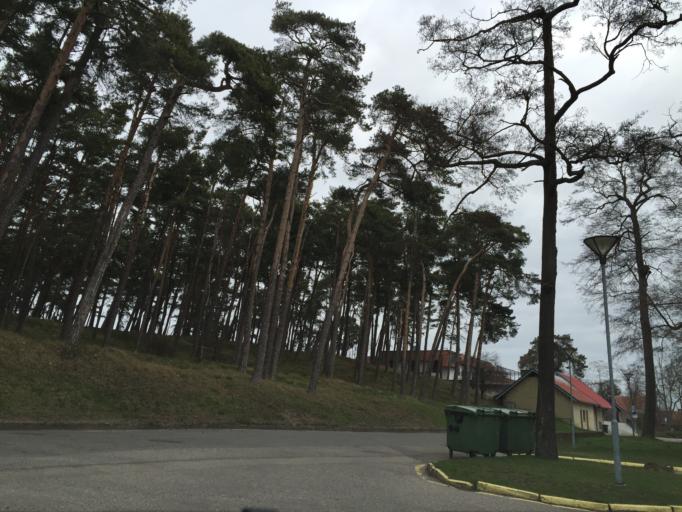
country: LT
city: Nida
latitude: 55.3045
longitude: 21.0051
